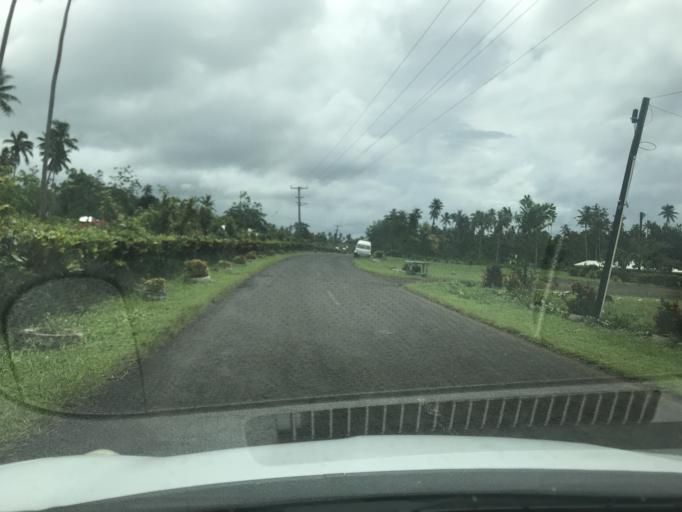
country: WS
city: Matavai
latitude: -14.0322
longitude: -171.6393
